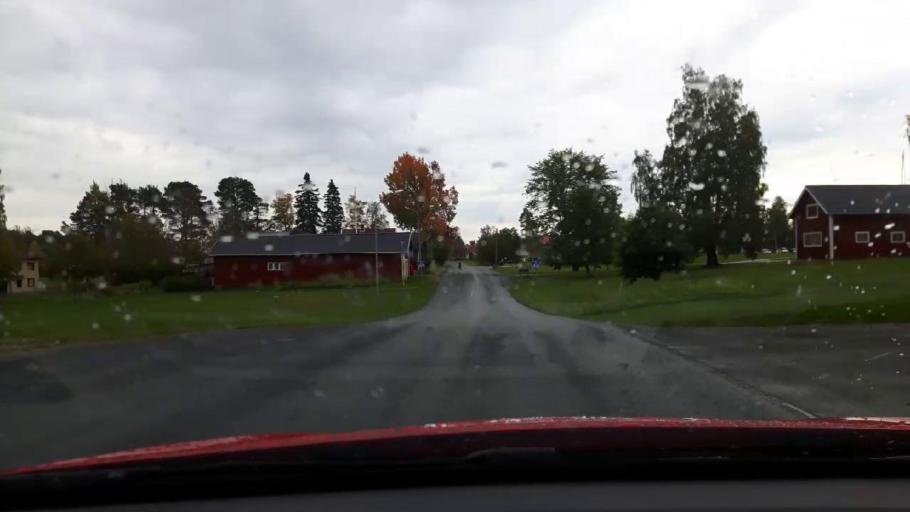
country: SE
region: Jaemtland
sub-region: Bergs Kommun
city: Hoverberg
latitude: 62.9236
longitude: 14.5162
